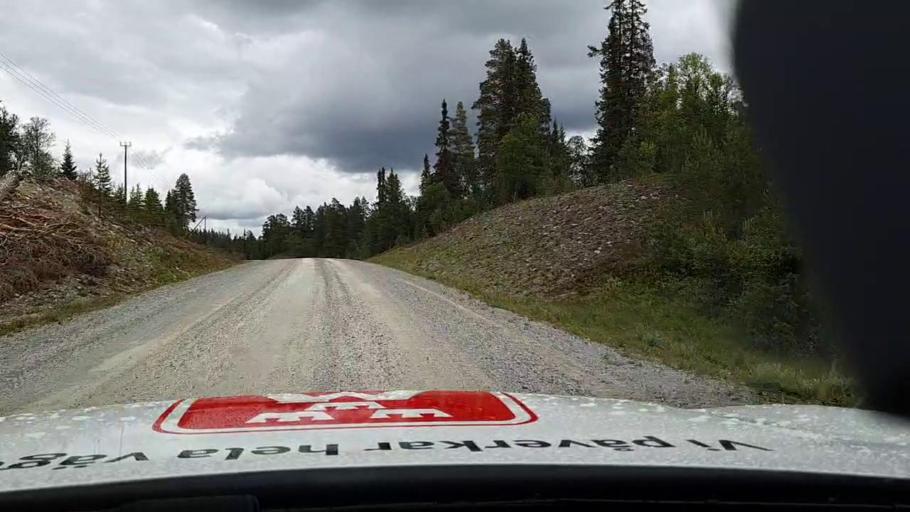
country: SE
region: Jaemtland
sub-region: Are Kommun
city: Are
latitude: 62.6652
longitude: 12.9306
